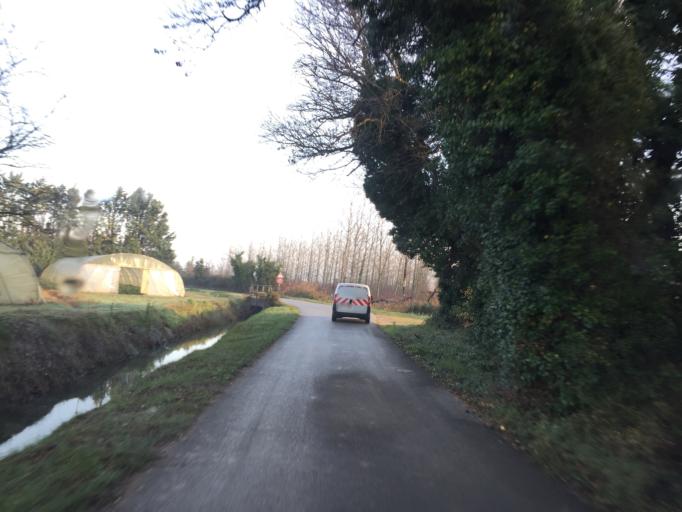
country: FR
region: Provence-Alpes-Cote d'Azur
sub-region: Departement du Vaucluse
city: Caderousse
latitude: 44.1113
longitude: 4.7584
